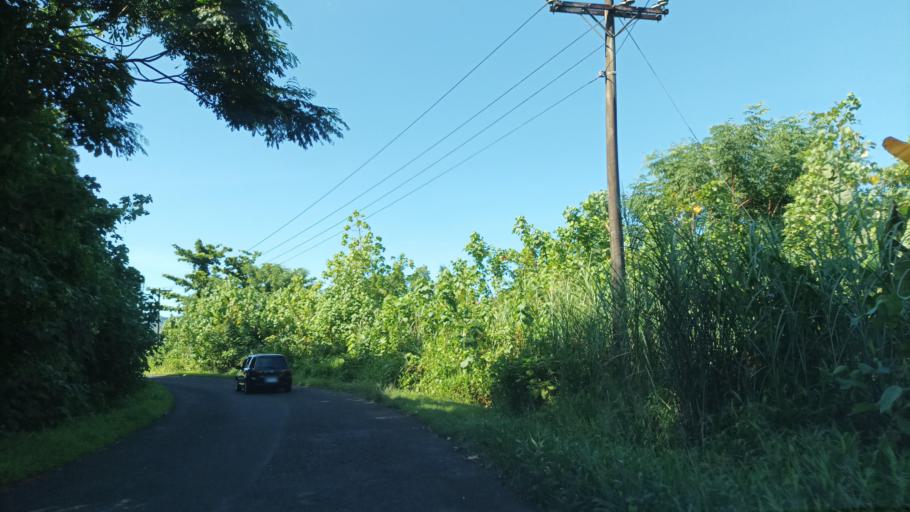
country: FM
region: Pohnpei
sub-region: Madolenihm Municipality
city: Madolenihm Municipality Government
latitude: 6.8607
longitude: 158.2937
